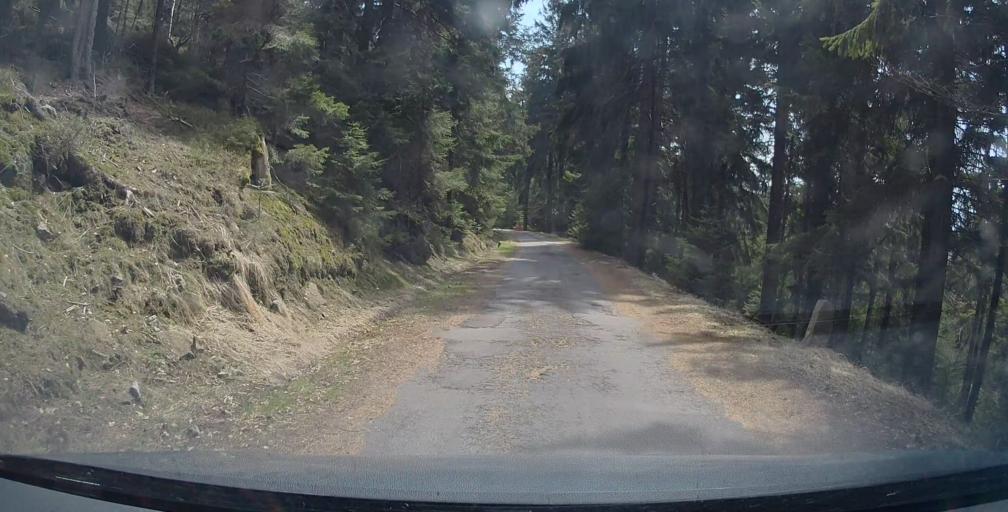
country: CZ
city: Machov
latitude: 50.4730
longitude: 16.2881
